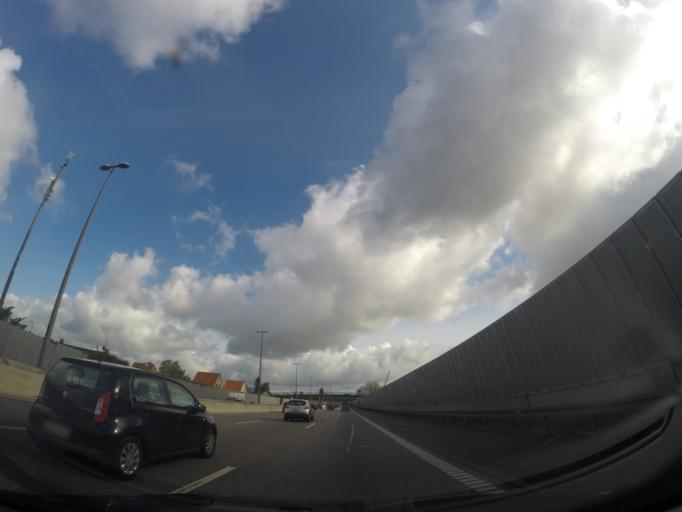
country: DK
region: Capital Region
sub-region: Rodovre Kommune
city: Rodovre
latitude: 55.7018
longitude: 12.4478
